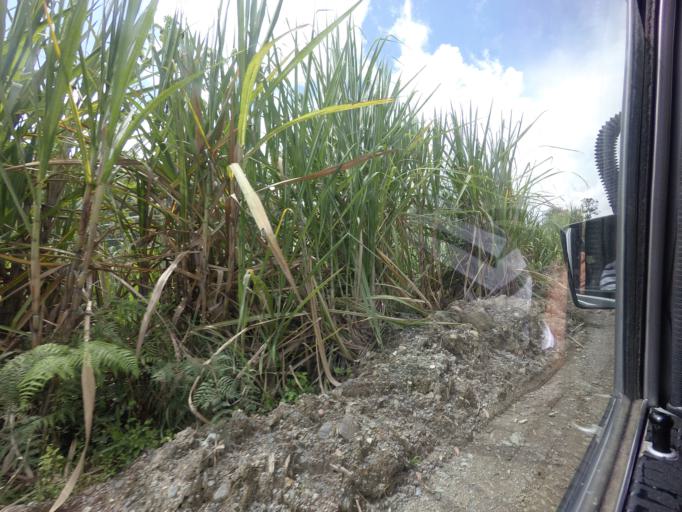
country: CO
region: Huila
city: Isnos
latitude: 1.9567
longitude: -76.2816
